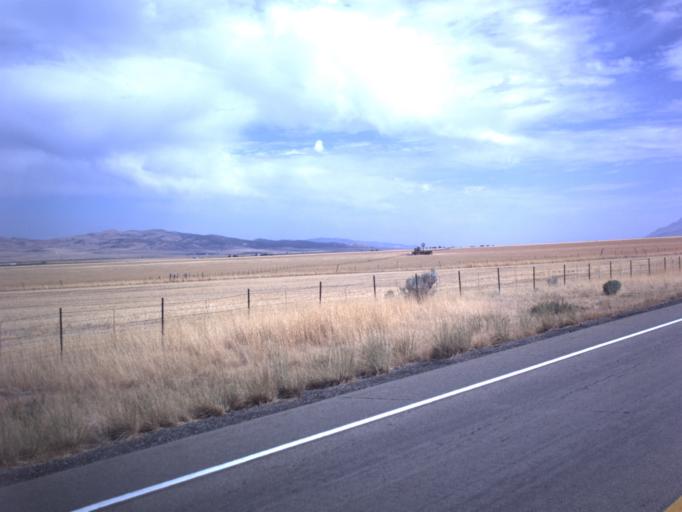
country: US
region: Utah
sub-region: Juab County
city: Nephi
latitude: 39.4946
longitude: -111.8799
